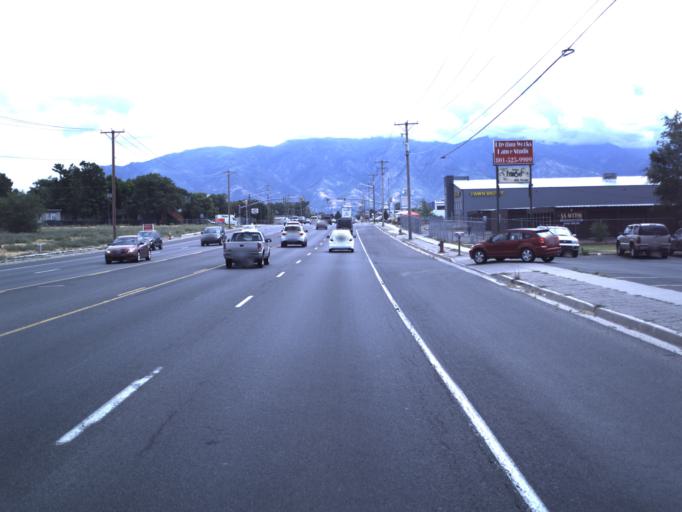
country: US
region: Utah
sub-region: Davis County
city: Clearfield
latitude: 41.0892
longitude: -112.0343
